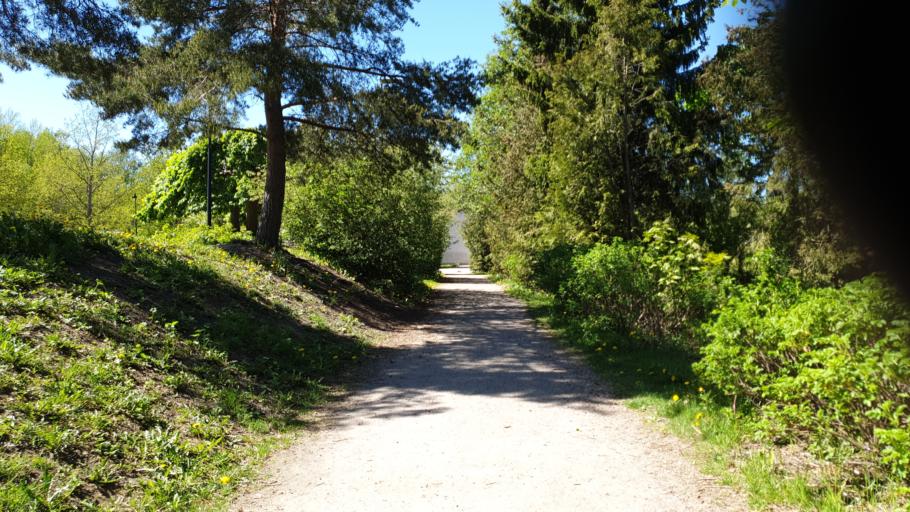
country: FI
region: Uusimaa
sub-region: Helsinki
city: Helsinki
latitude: 60.2546
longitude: 24.9327
